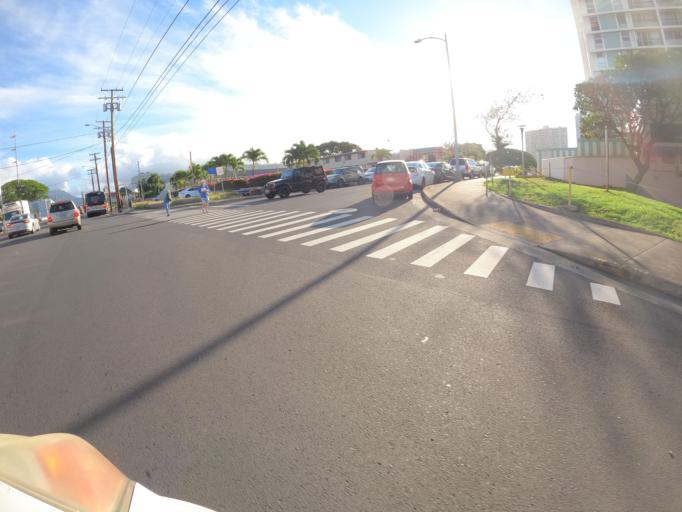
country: US
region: Hawaii
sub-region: Honolulu County
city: Honolulu
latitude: 21.3205
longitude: -157.8614
